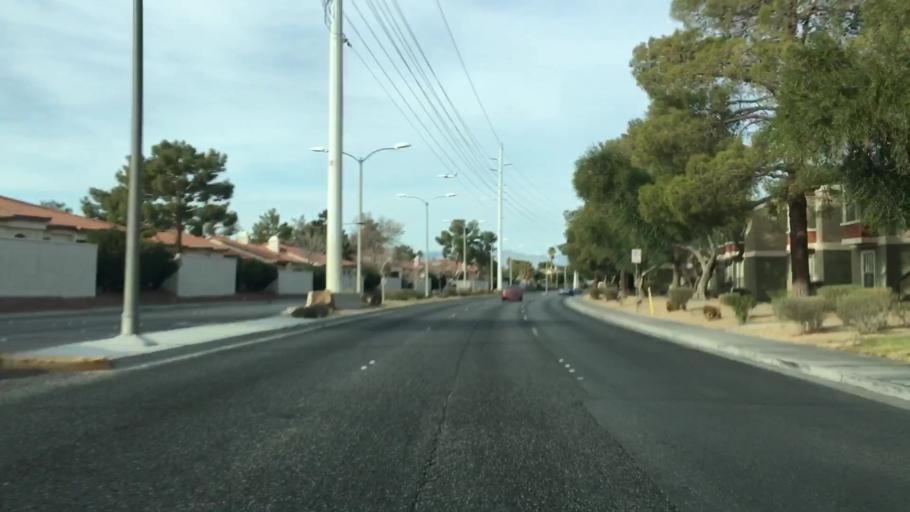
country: US
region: Nevada
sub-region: Clark County
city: Whitney
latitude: 36.0577
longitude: -115.0846
